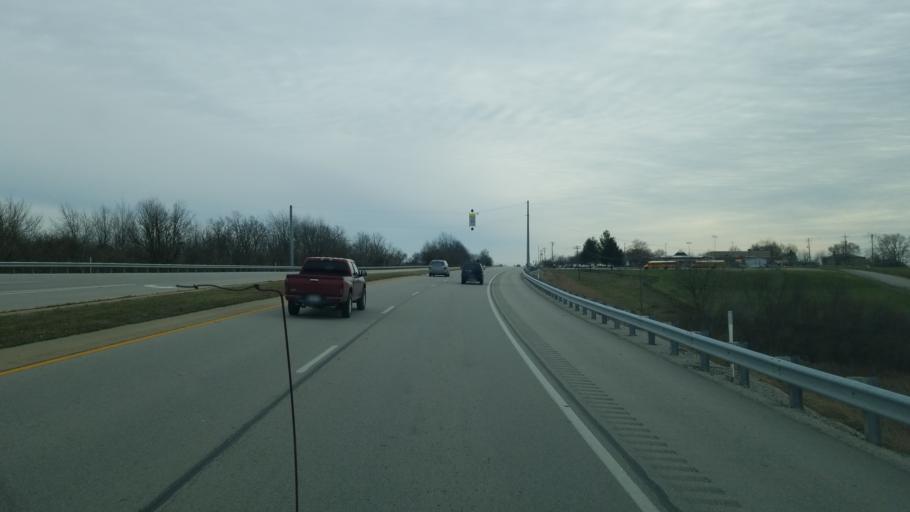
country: US
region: Kentucky
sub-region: Bourbon County
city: Paris
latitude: 38.2266
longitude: -84.2462
